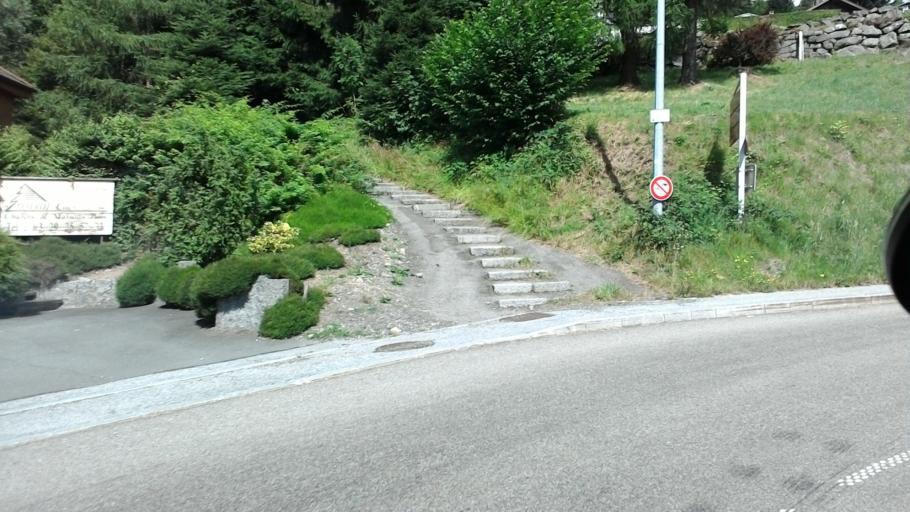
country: FR
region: Lorraine
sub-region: Departement des Vosges
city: La Bresse
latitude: 48.0042
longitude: 6.8715
